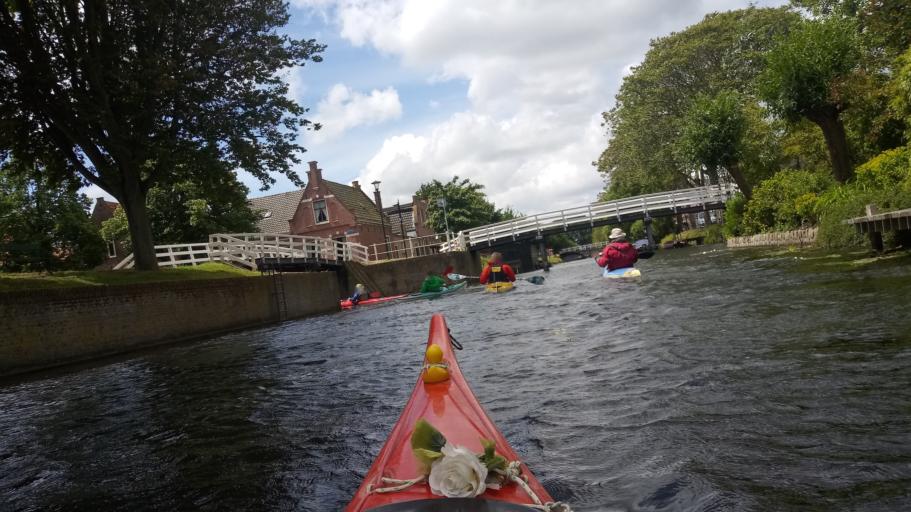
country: NL
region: North Holland
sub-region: Gemeente Enkhuizen
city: Enkhuizen
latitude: 52.7032
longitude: 5.2844
